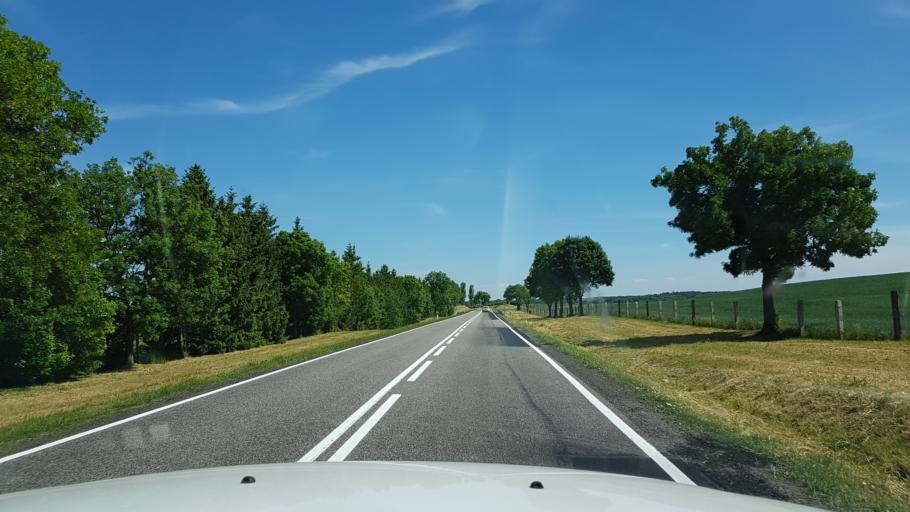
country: PL
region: West Pomeranian Voivodeship
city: Trzcinsko Zdroj
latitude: 52.9602
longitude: 14.5236
